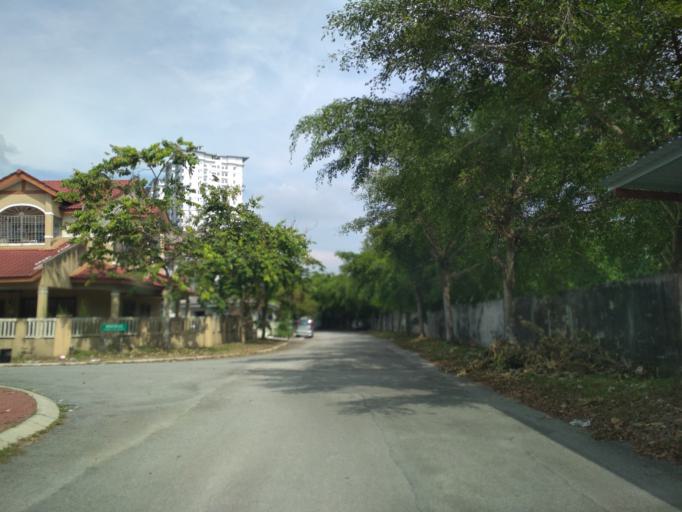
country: MY
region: Perak
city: Kampar
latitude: 4.3295
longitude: 101.1304
